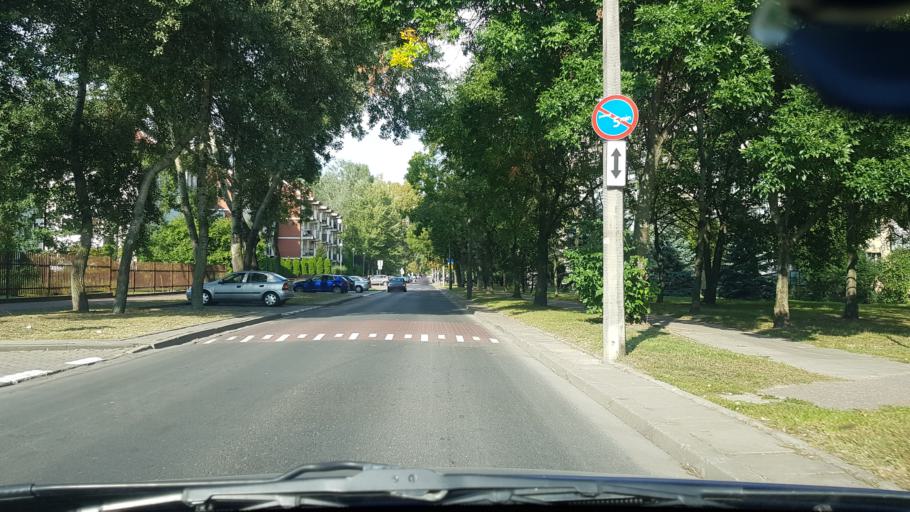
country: PL
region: Masovian Voivodeship
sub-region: Warszawa
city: Bielany
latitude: 52.2803
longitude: 20.9348
